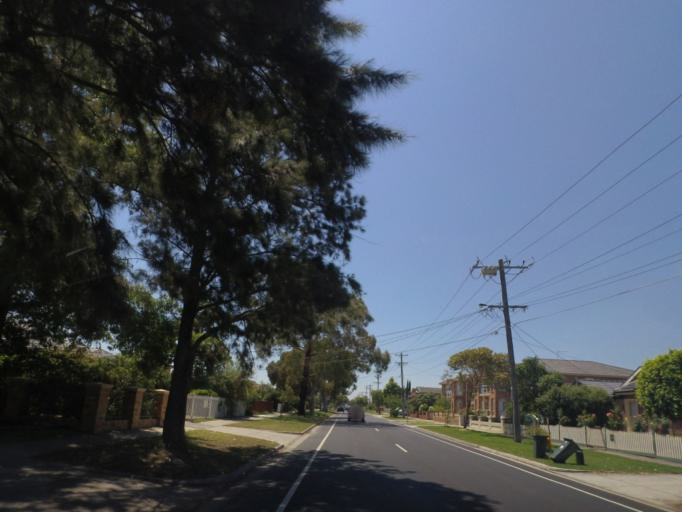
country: AU
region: Victoria
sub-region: Moreland
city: Oak Park
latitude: -37.7139
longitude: 144.9236
